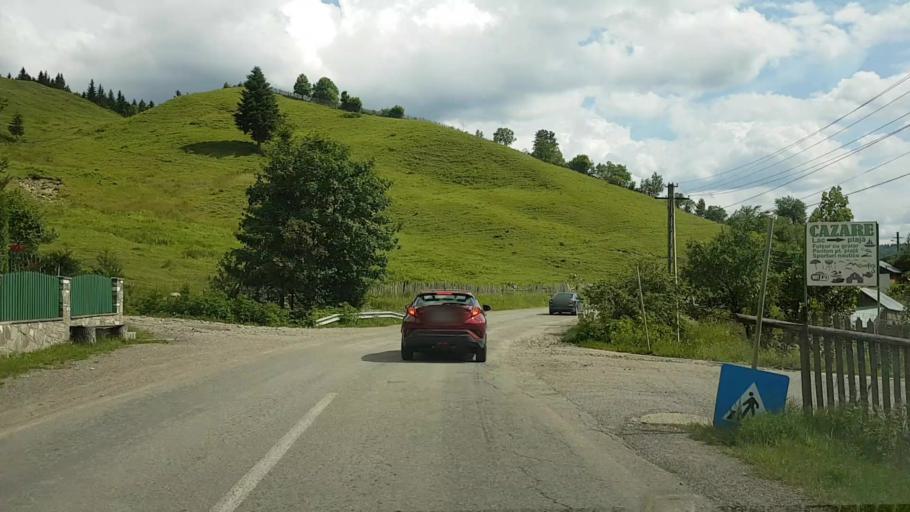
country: RO
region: Neamt
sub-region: Comuna Bicaz
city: Dodeni
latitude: 47.0043
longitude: 26.0981
